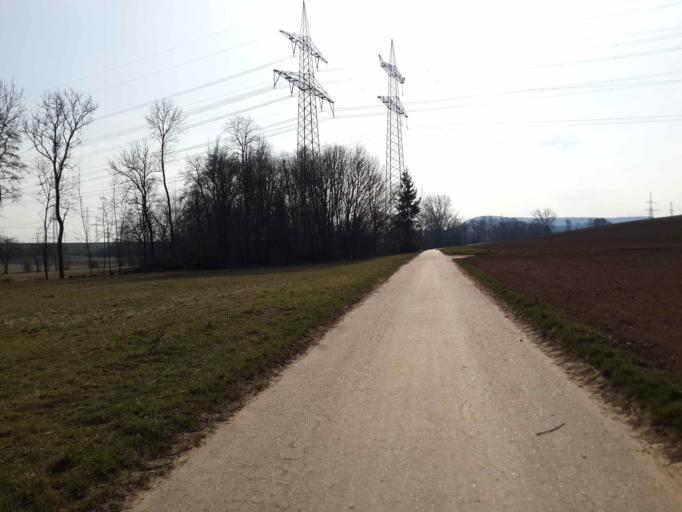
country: DE
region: Baden-Wuerttemberg
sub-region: Regierungsbezirk Stuttgart
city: Leingarten
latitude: 49.1480
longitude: 9.1470
